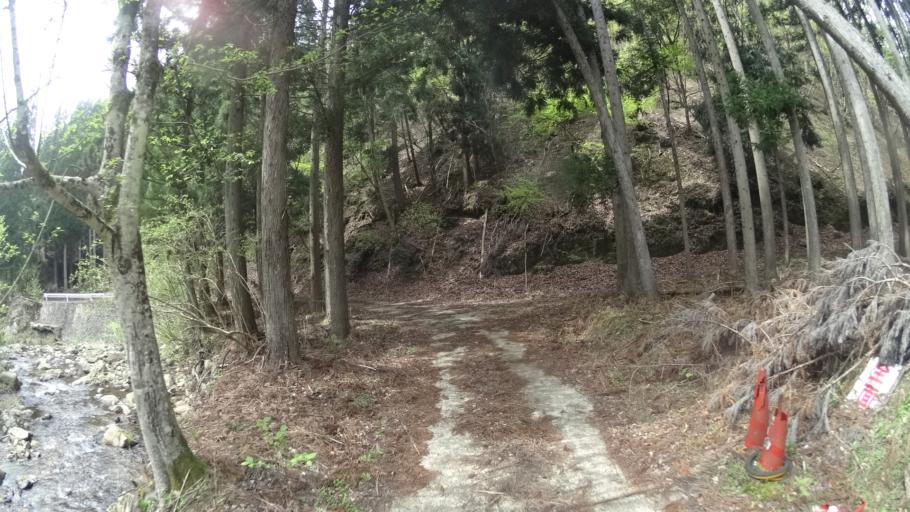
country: JP
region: Kyoto
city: Maizuru
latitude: 35.4066
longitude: 135.5112
